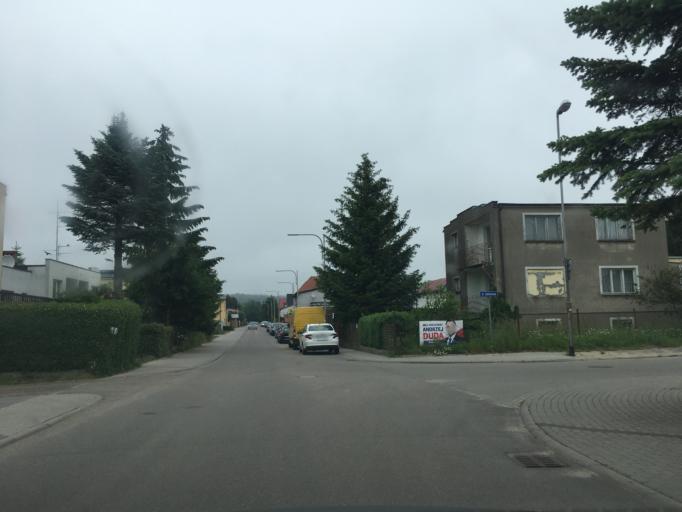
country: PL
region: West Pomeranian Voivodeship
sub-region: Koszalin
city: Koszalin
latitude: 54.1870
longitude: 16.2162
